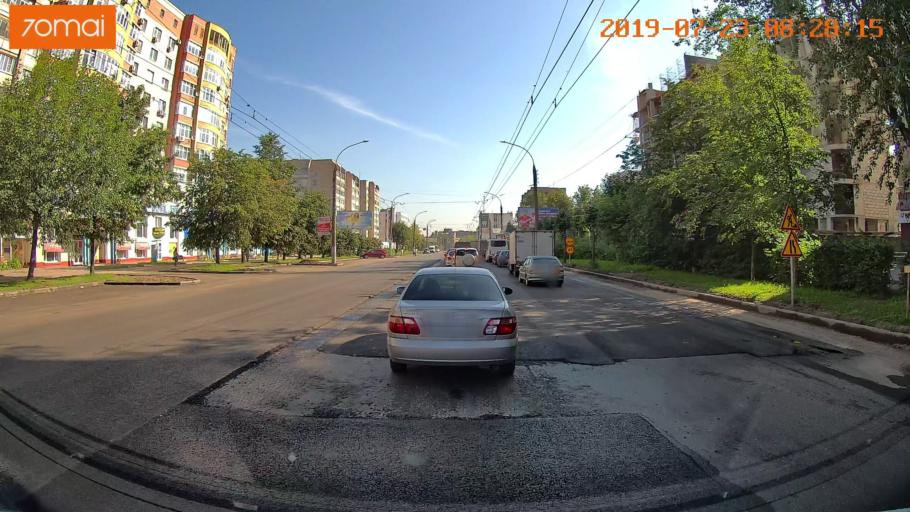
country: RU
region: Ivanovo
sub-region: Gorod Ivanovo
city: Ivanovo
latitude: 56.9898
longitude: 40.9704
